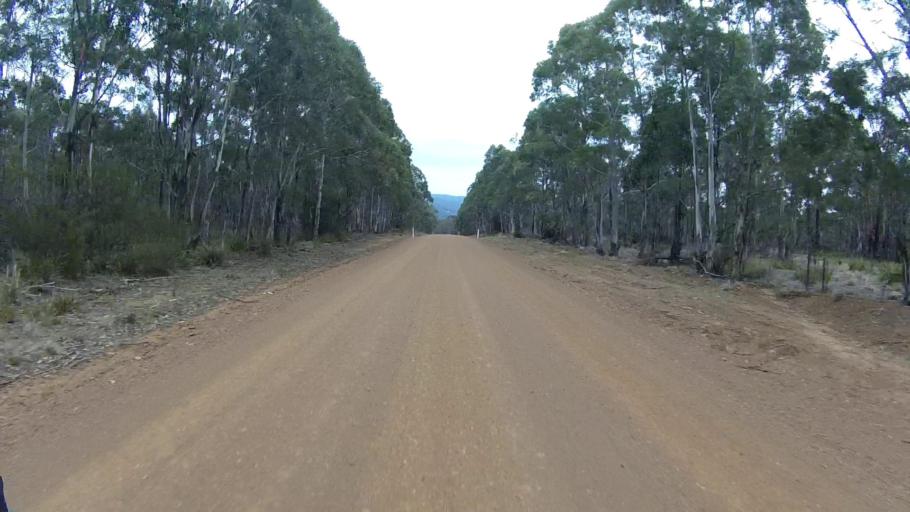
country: AU
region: Tasmania
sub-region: Sorell
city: Sorell
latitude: -42.5818
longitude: 147.8811
